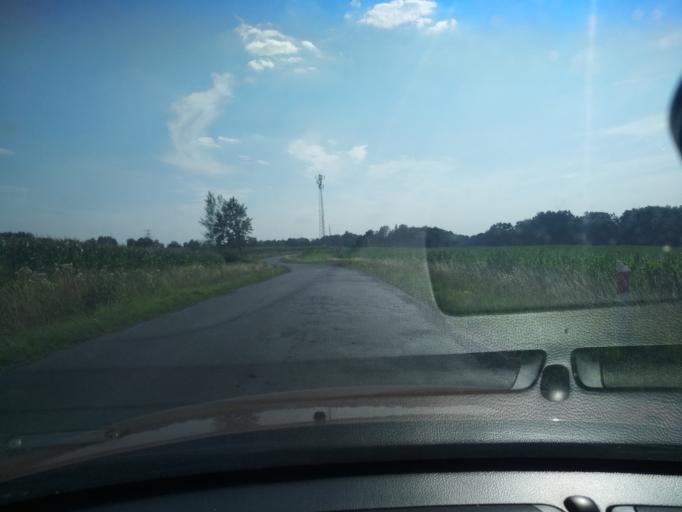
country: PL
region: Lower Silesian Voivodeship
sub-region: Powiat zgorzelecki
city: Sulikow
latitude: 51.0833
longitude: 15.1279
